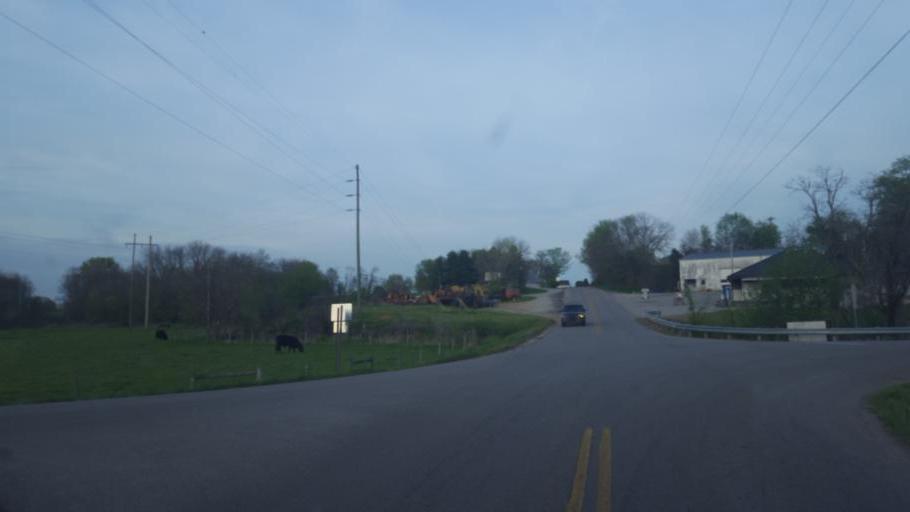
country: US
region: Kentucky
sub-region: Metcalfe County
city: Edmonton
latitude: 37.0784
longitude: -85.6966
